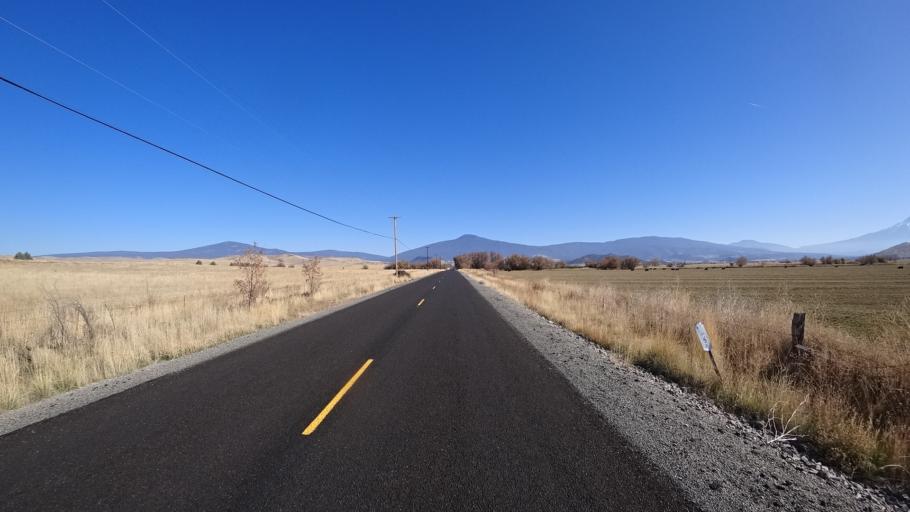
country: US
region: California
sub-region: Siskiyou County
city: Montague
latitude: 41.7263
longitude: -122.4232
